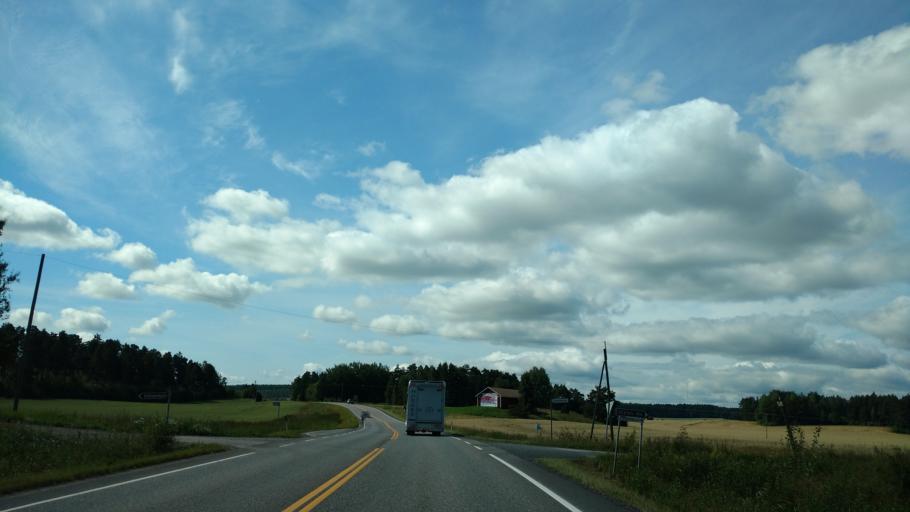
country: FI
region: Varsinais-Suomi
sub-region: Salo
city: Pernioe
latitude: 60.2146
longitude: 23.1137
